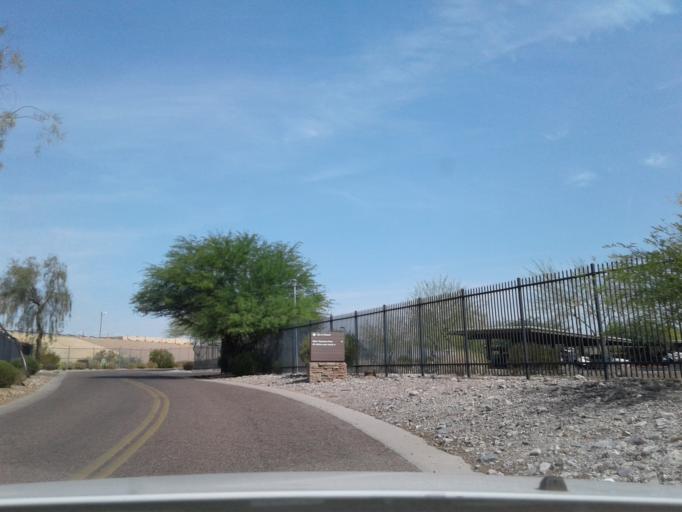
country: US
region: Arizona
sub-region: Maricopa County
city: Paradise Valley
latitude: 33.5273
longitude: -112.0306
